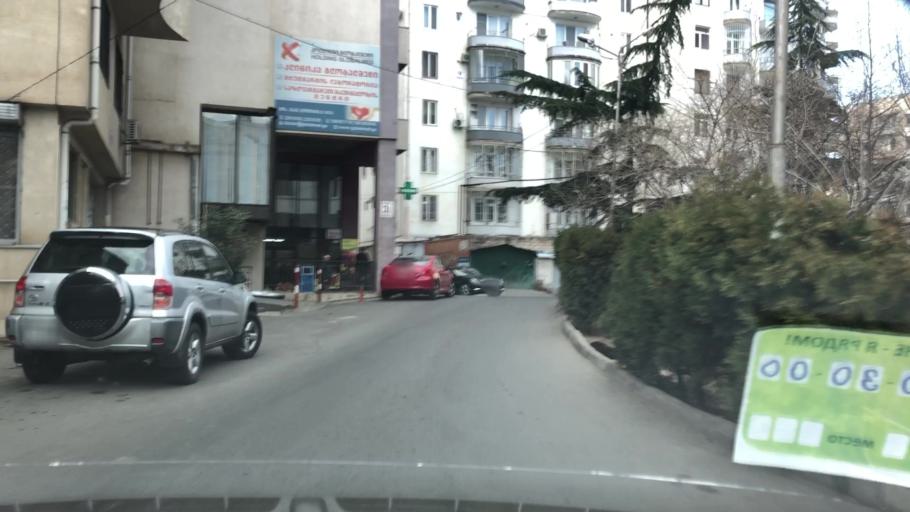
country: GE
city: Tsqnet'i
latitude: 41.7133
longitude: 44.7607
